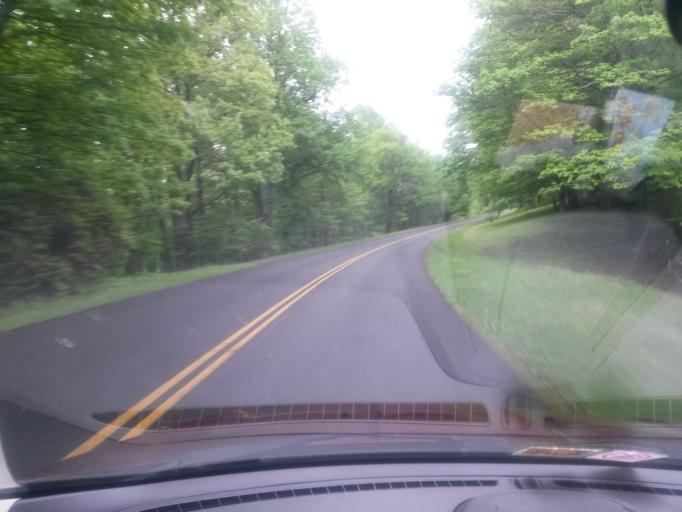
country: US
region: Virginia
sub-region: Floyd County
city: Floyd
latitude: 36.8310
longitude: -80.3294
